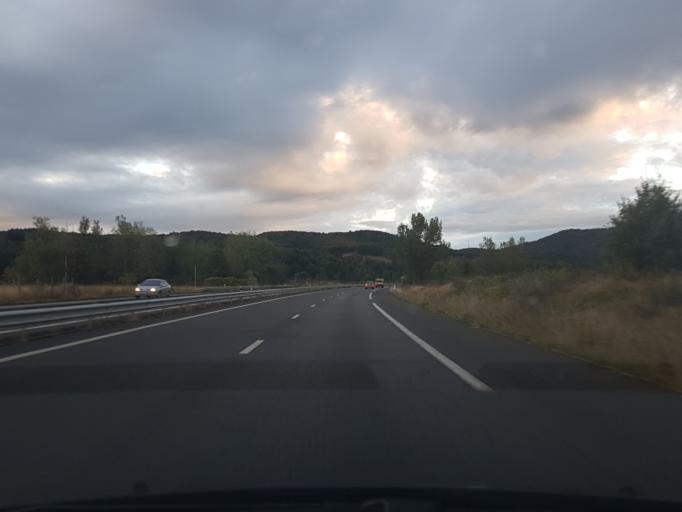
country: FR
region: Midi-Pyrenees
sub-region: Departement de l'Ariege
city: Varilhes
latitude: 43.0548
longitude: 1.6494
